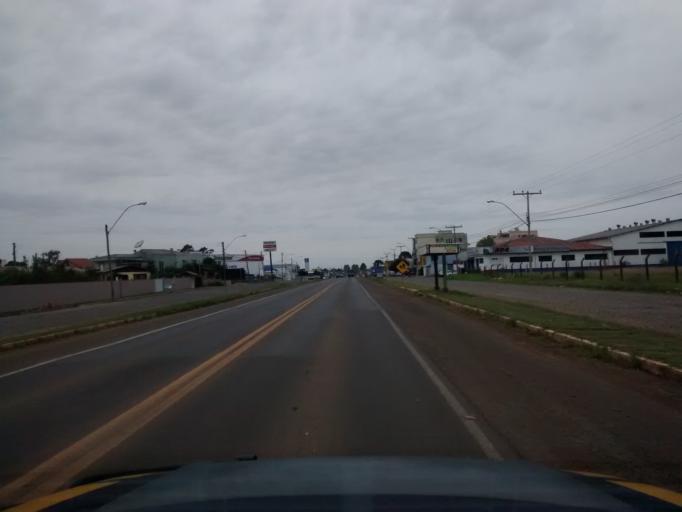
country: BR
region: Rio Grande do Sul
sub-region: Vacaria
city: Vacaria
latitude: -28.5130
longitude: -50.9334
